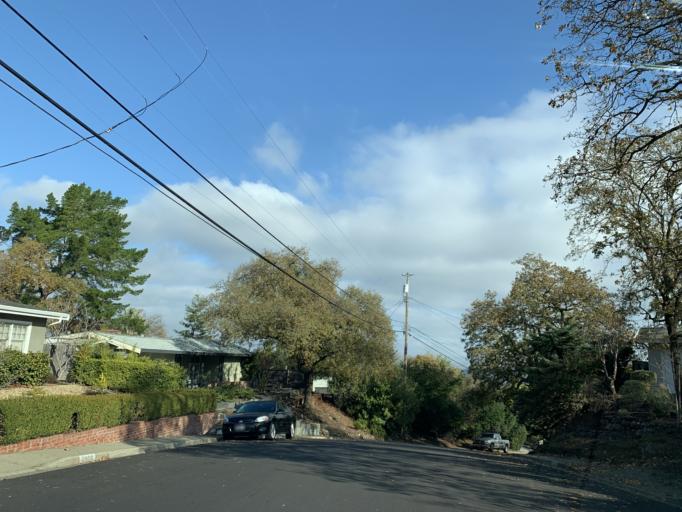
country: US
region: California
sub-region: Contra Costa County
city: Saranap
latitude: 37.8830
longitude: -122.0708
